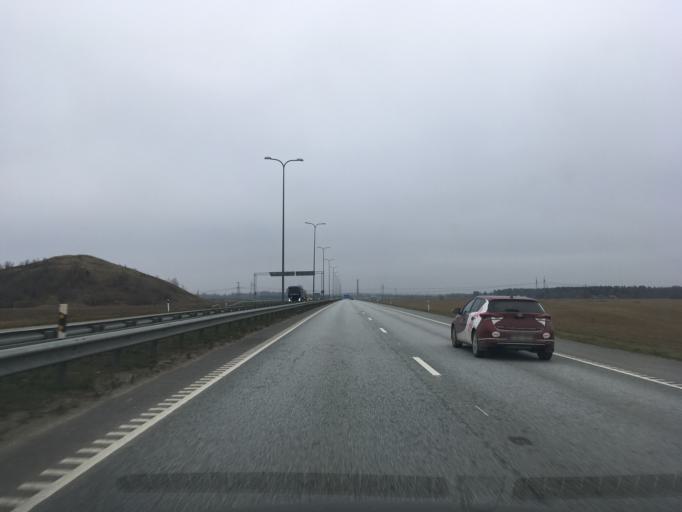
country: EE
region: Ida-Virumaa
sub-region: Kohtla-Jaerve linn
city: Kohtla-Jarve
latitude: 59.3973
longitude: 27.3337
